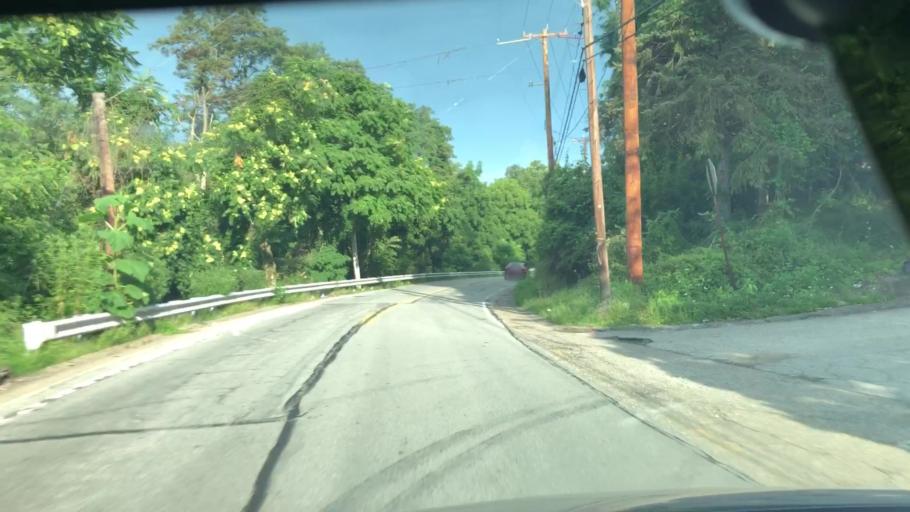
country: US
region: Pennsylvania
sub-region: Allegheny County
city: Blawnox
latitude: 40.4766
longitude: -79.8689
